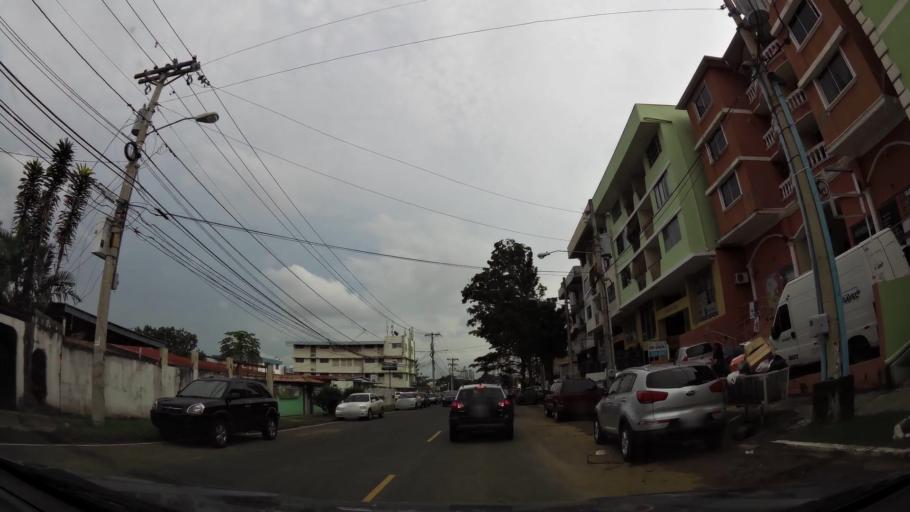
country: PA
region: Panama
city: Panama
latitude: 9.0111
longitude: -79.5271
